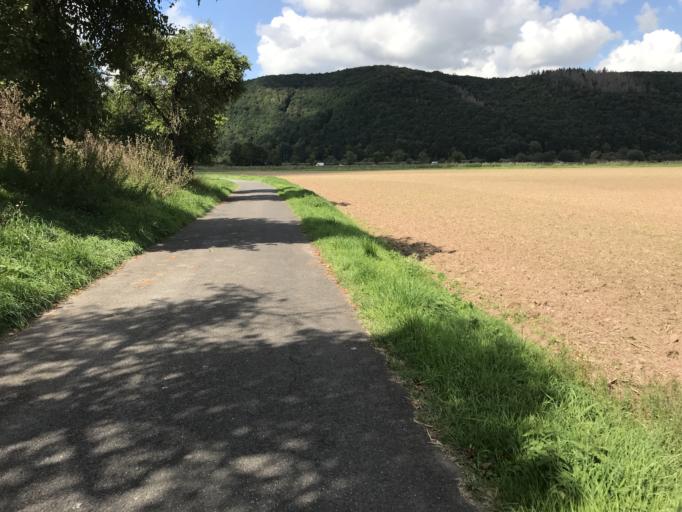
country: DE
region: Hesse
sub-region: Regierungsbezirk Kassel
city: Bad Sooden-Allendorf
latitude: 51.2837
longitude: 9.9717
